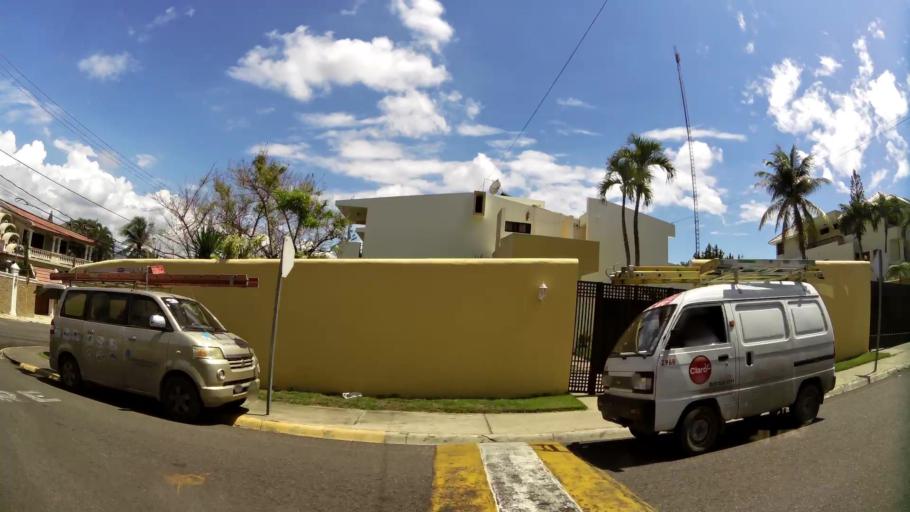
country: DO
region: Santiago
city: Santiago de los Caballeros
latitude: 19.4679
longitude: -70.6803
